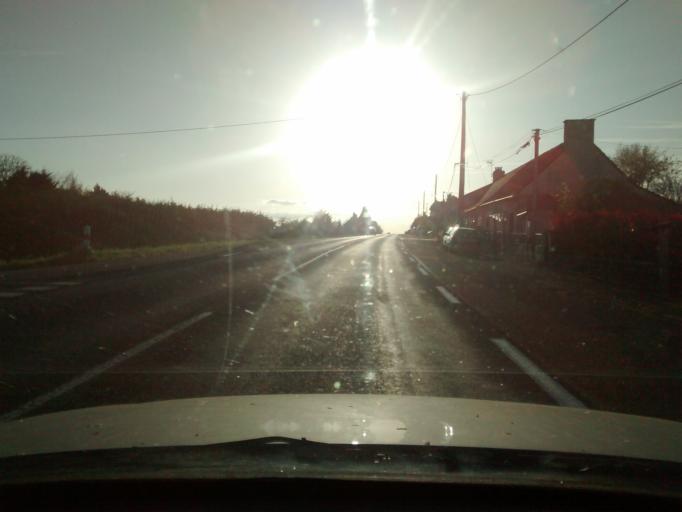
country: FR
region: Pays de la Loire
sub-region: Departement de la Sarthe
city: Coulans-sur-Gee
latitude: 48.0176
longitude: -0.0205
